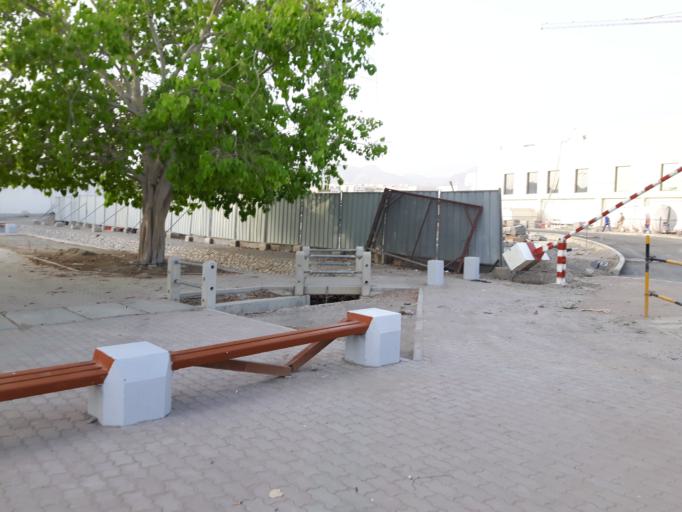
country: OM
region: Muhafazat Masqat
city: Bawshar
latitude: 23.6175
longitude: 58.4673
